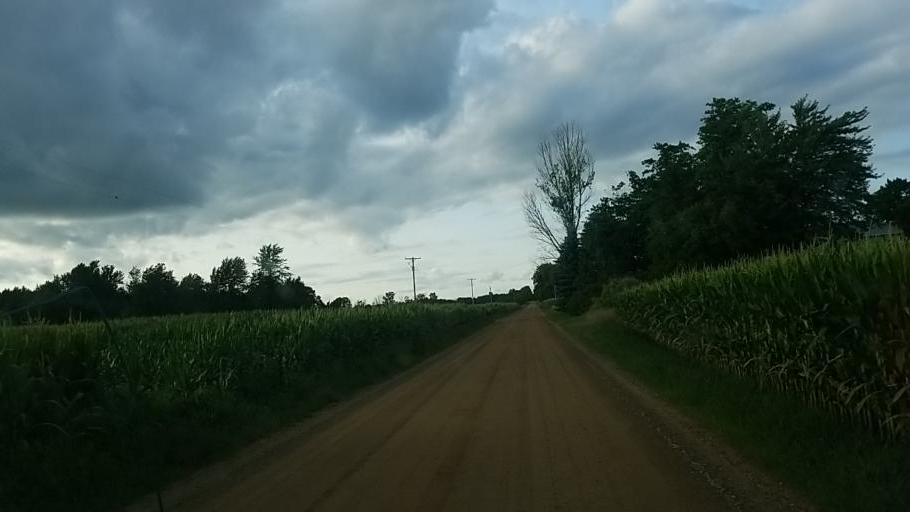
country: US
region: Michigan
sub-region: Montcalm County
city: Howard City
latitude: 43.3311
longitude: -85.3830
